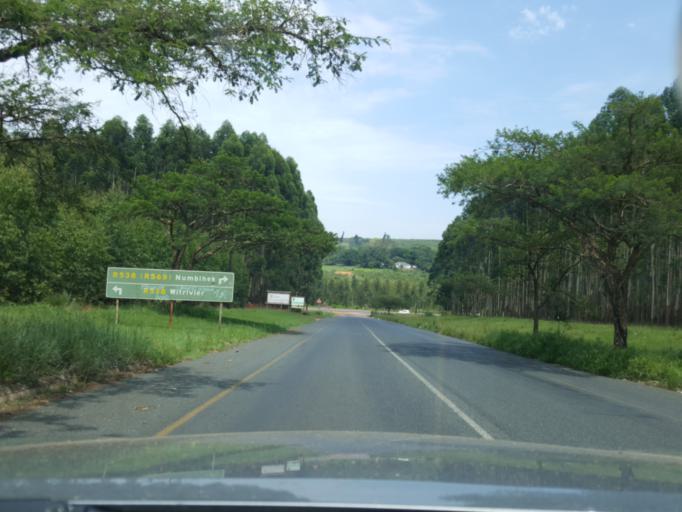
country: ZA
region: Mpumalanga
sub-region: Ehlanzeni District
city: White River
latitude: -25.3014
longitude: 31.0472
